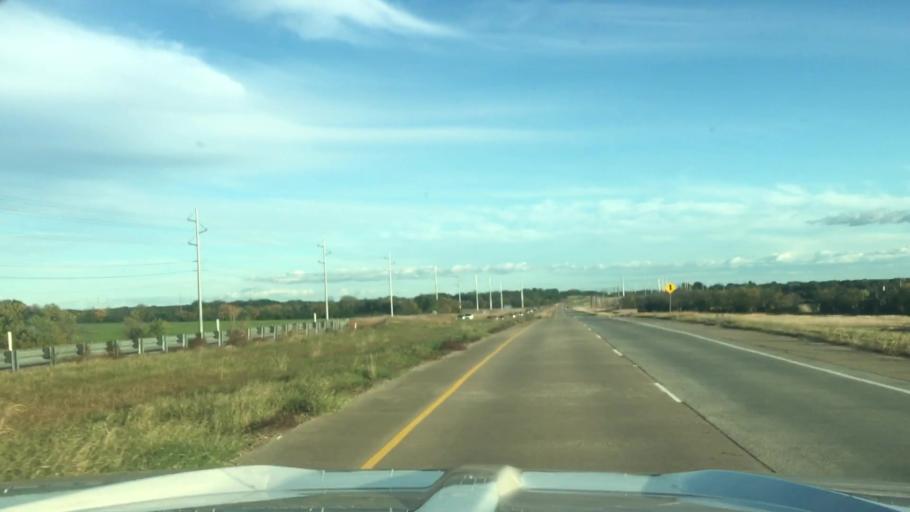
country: US
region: Texas
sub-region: Denton County
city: Denton
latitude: 33.2576
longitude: -97.1092
